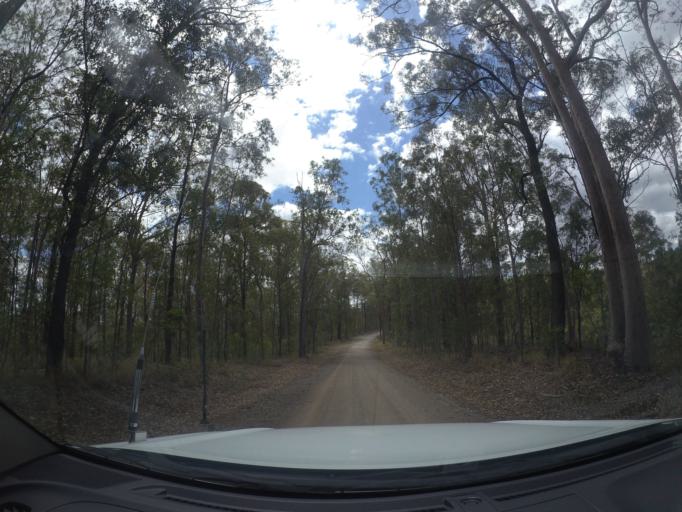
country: AU
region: Queensland
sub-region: Logan
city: Cedar Vale
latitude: -27.9091
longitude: 153.0312
